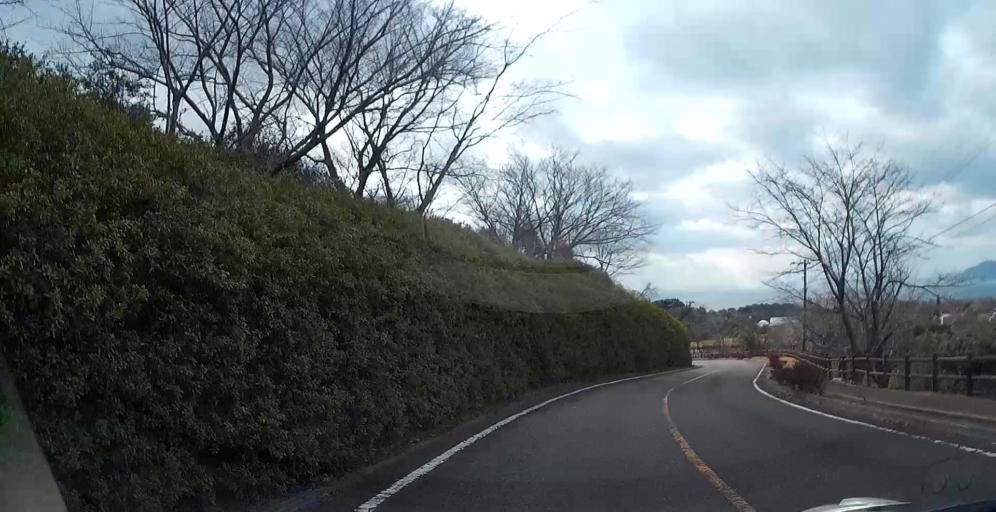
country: JP
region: Kumamoto
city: Yatsushiro
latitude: 32.3677
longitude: 130.4960
